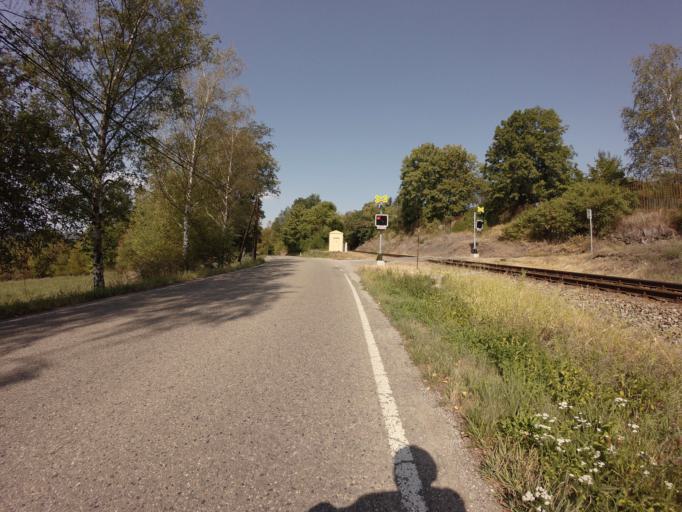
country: CZ
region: Central Bohemia
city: Kamenny Privoz
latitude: 49.8611
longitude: 14.5404
